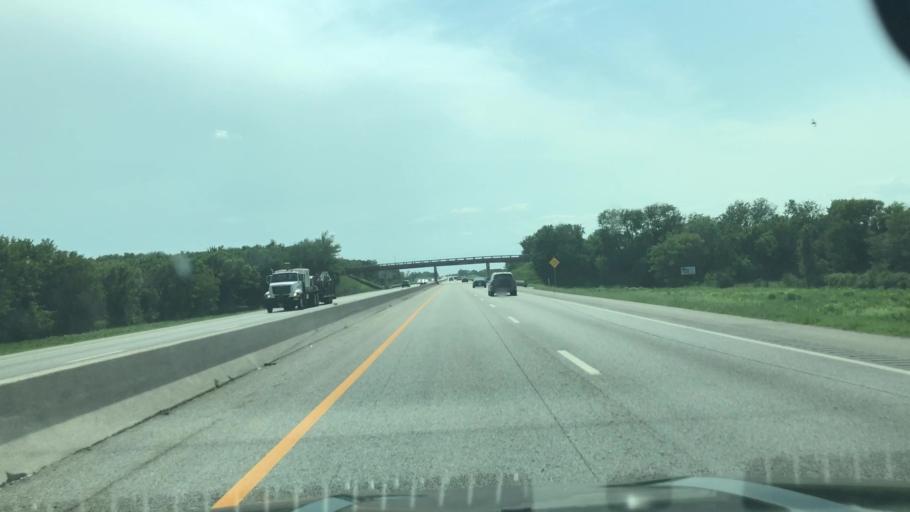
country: US
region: Oklahoma
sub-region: Ottawa County
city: Afton
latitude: 36.7131
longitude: -94.9613
